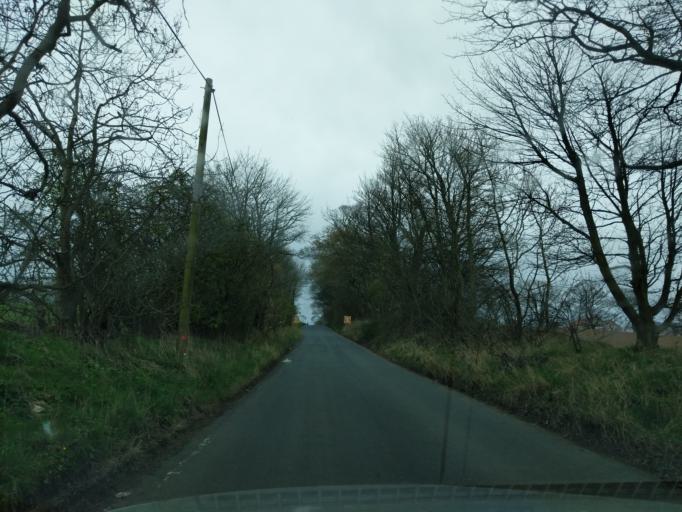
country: GB
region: Scotland
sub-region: Edinburgh
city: Balerno
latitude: 55.8924
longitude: -3.3471
